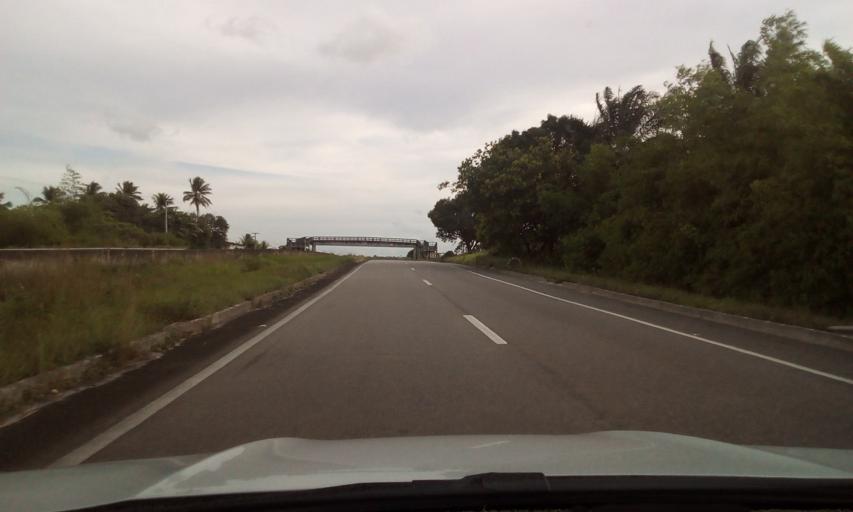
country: BR
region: Paraiba
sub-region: Alhandra
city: Alhandra
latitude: -7.3987
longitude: -34.9554
